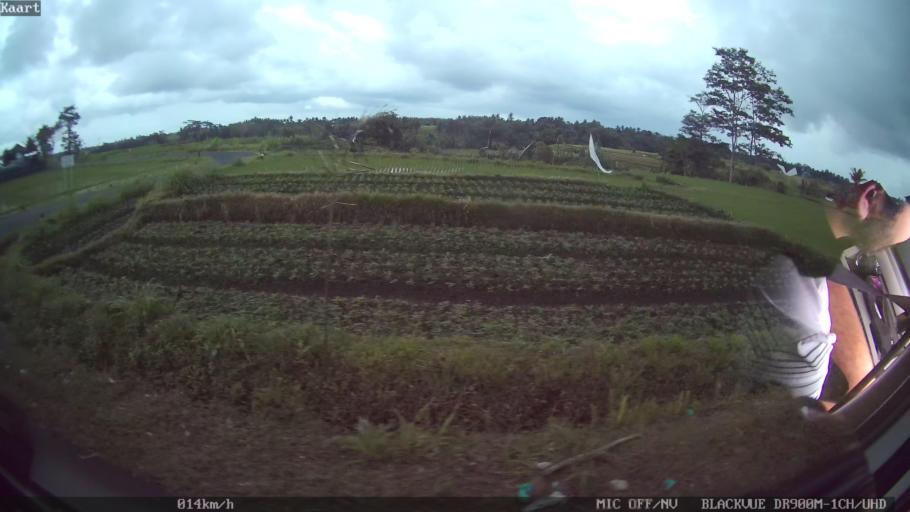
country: ID
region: Bali
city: Banjar Cemenggon
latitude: -8.5290
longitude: 115.1953
